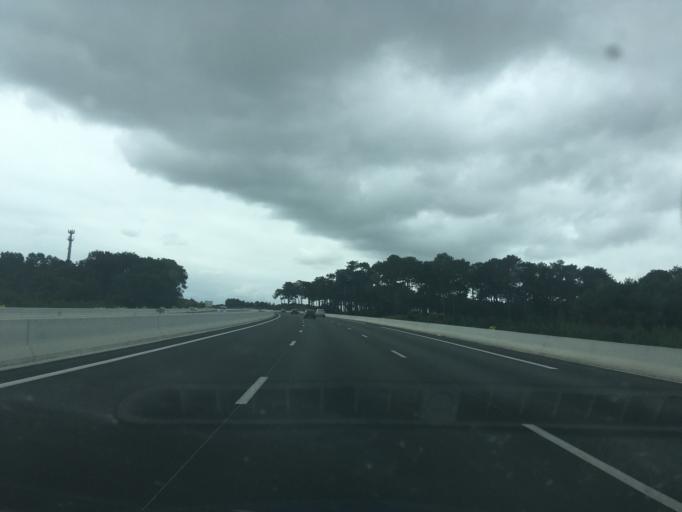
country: FR
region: Aquitaine
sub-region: Departement des Landes
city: Labenne
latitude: 43.6067
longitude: -1.4160
